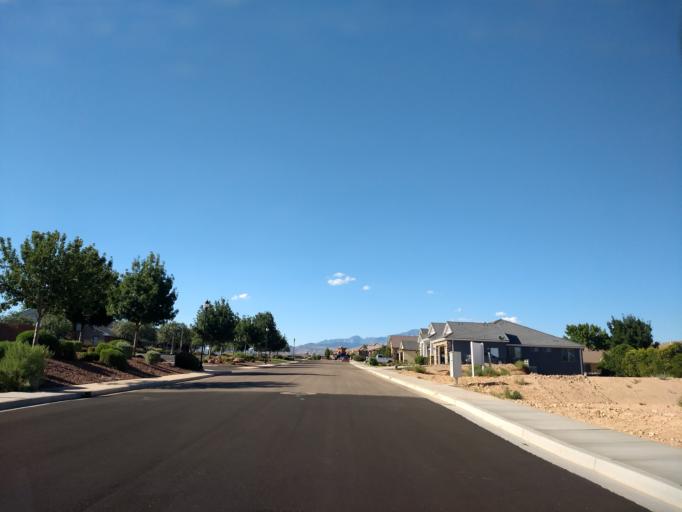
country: US
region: Utah
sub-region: Washington County
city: Saint George
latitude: 37.0913
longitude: -113.5468
